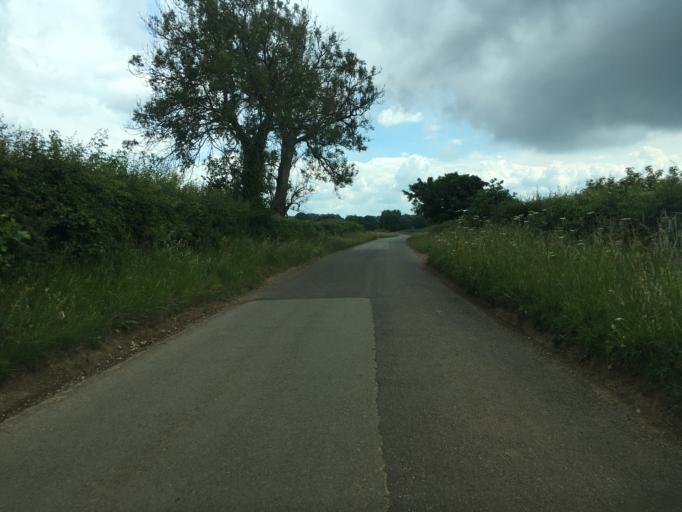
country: GB
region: England
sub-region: Gloucestershire
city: Coates
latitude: 51.7608
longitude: -2.0615
